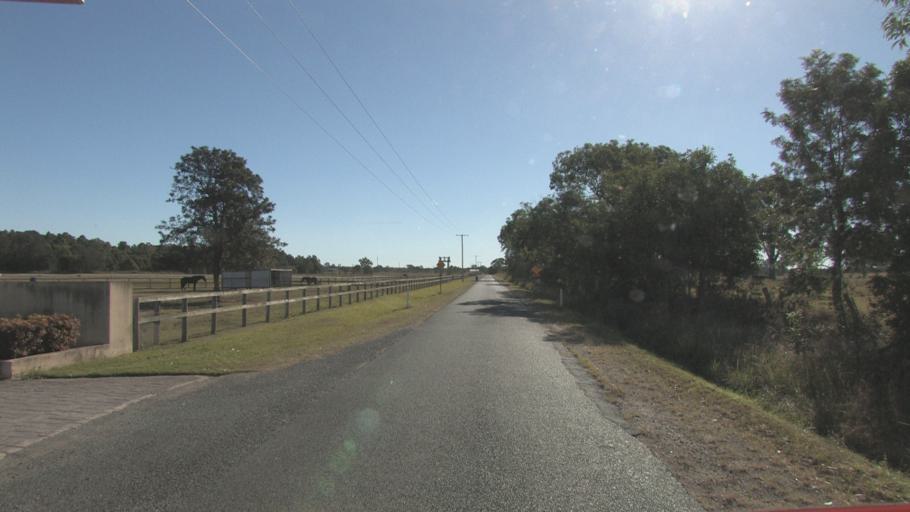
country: AU
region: Queensland
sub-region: Logan
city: Chambers Flat
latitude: -27.7693
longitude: 153.0666
